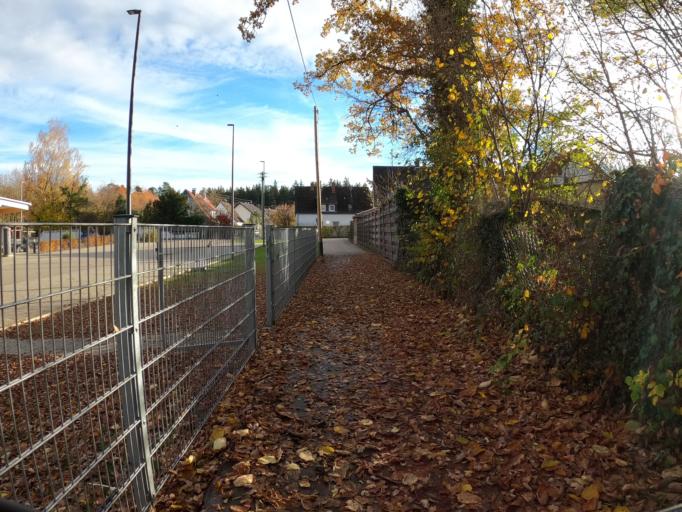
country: DE
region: Bavaria
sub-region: Swabia
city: Nersingen
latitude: 48.4133
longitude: 10.1532
